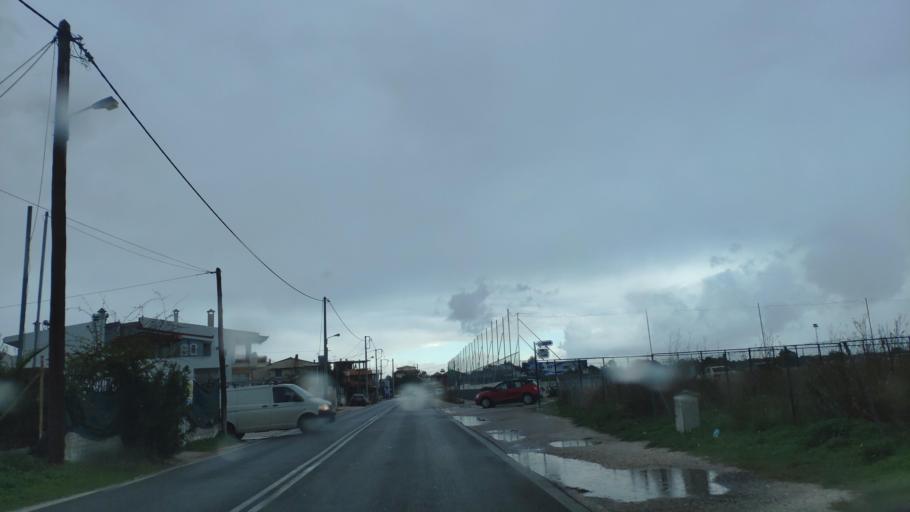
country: GR
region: Attica
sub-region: Nomarchia Anatolikis Attikis
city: Artemida
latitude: 37.9863
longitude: 24.0128
